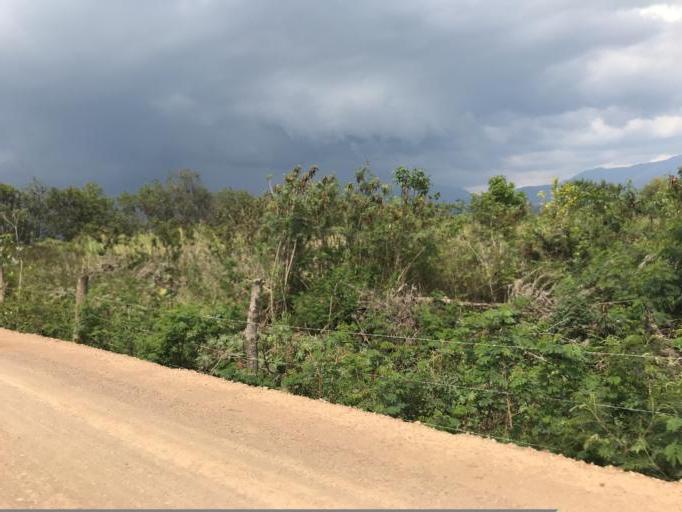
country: CO
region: Boyaca
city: Villa de Leiva
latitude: 5.6571
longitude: -73.5863
